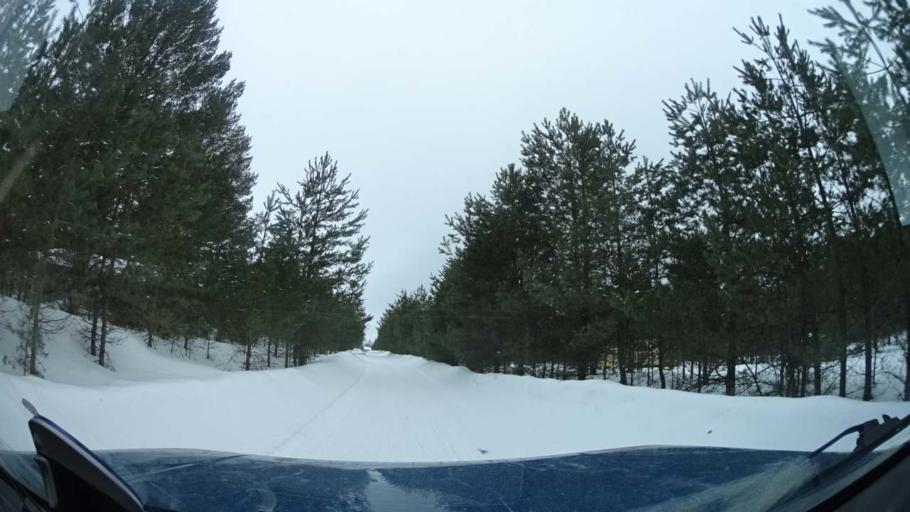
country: RU
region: Tverskaya
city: Radchenko
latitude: 56.7051
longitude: 36.4027
